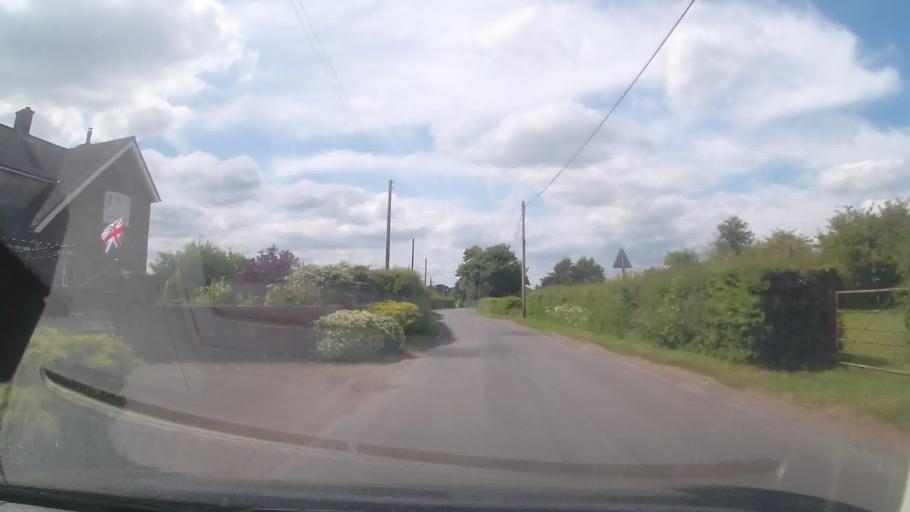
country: GB
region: England
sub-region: Shropshire
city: Stoke upon Tern
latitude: 52.7934
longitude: -2.5566
